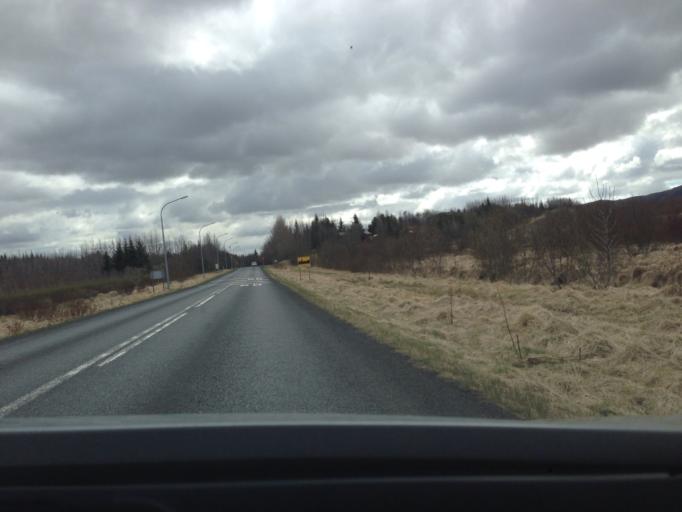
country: IS
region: South
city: Selfoss
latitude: 64.1207
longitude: -20.5037
